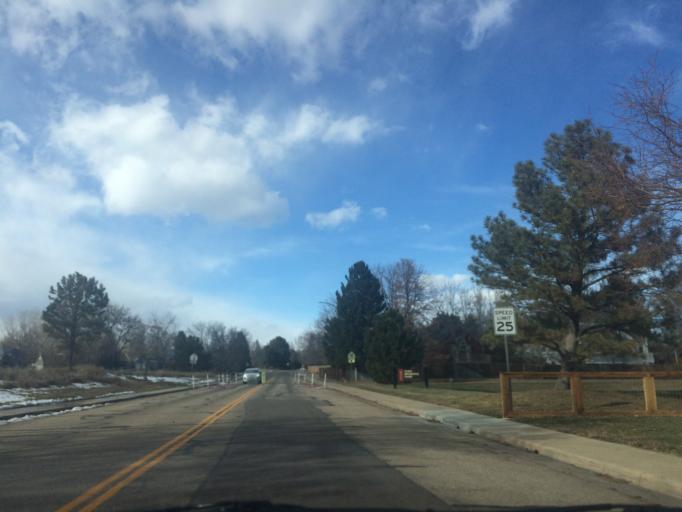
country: US
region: Colorado
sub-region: Boulder County
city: Louisville
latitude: 39.9726
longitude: -105.1404
